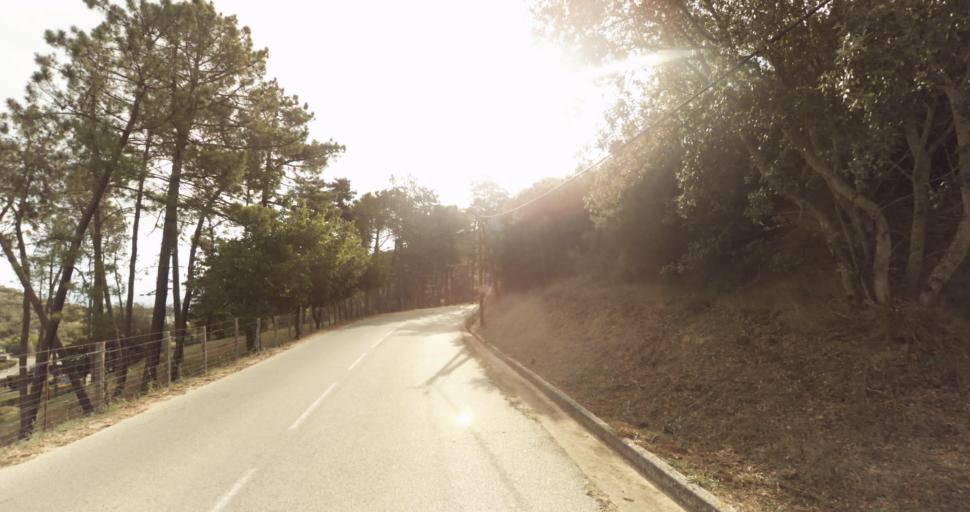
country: FR
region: Corsica
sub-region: Departement de la Corse-du-Sud
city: Ajaccio
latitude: 41.9305
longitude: 8.7117
